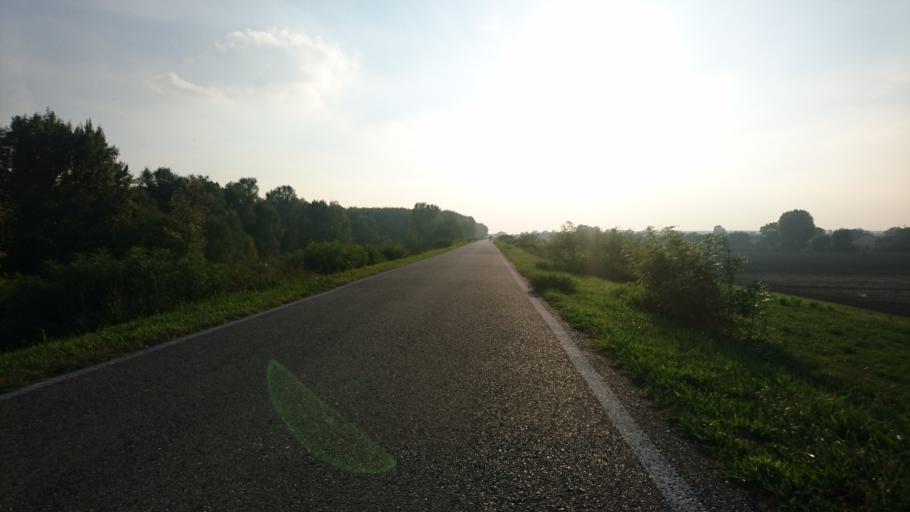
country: IT
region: Emilia-Romagna
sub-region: Provincia di Ferrara
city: Francolino
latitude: 44.8974
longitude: 11.6351
